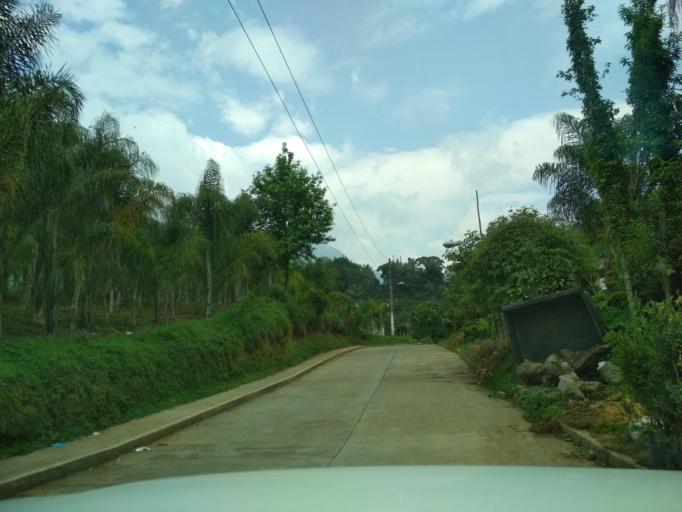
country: MX
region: Veracruz
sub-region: La Perla
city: La Perla
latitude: 18.9289
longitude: -97.1294
